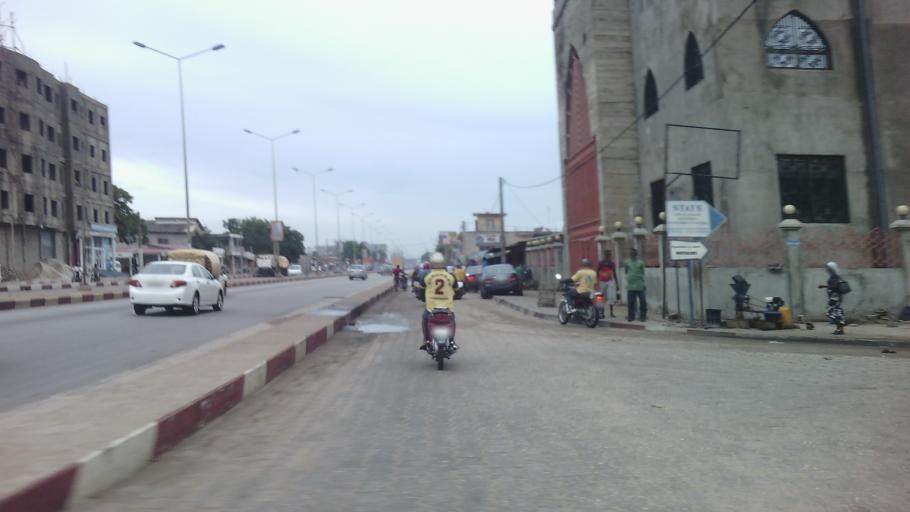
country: BJ
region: Littoral
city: Cotonou
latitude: 6.3655
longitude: 2.4165
